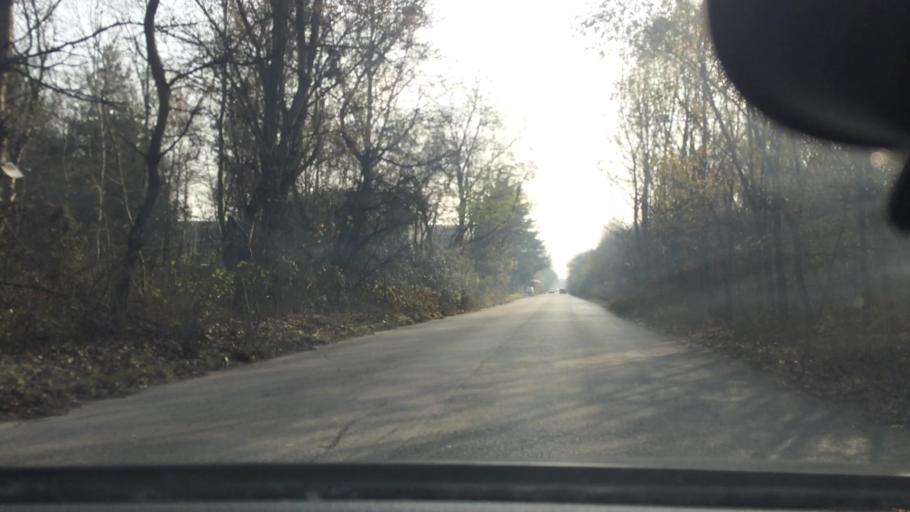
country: IT
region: Lombardy
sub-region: Citta metropolitana di Milano
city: Solaro
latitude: 45.6055
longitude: 9.0950
